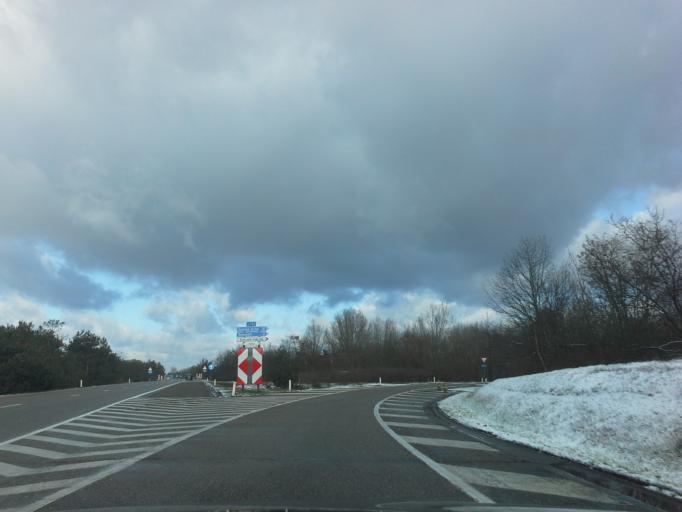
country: BE
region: Flanders
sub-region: Provincie Limburg
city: Overpelt
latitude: 51.2298
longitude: 5.4060
